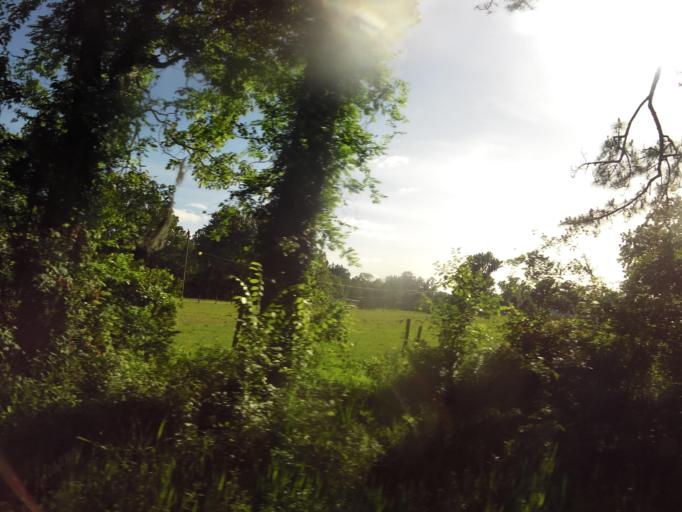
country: US
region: Florida
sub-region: Nassau County
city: Nassau Village-Ratliff
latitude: 30.4634
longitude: -81.8339
